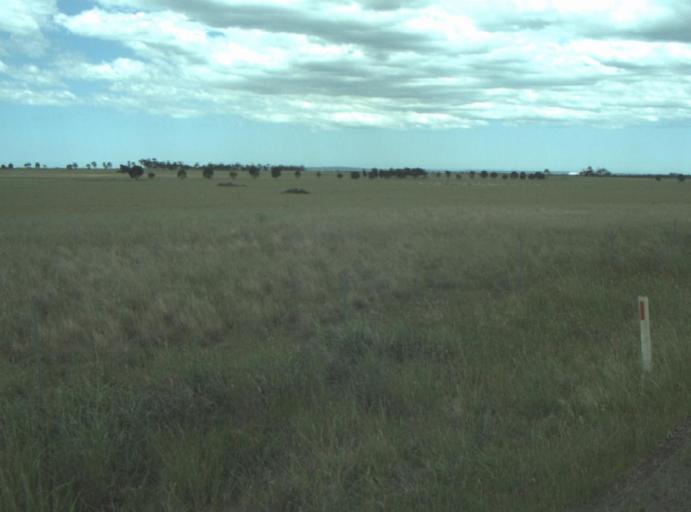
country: AU
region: Victoria
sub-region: Wyndham
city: Little River
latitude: -37.9611
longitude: 144.4633
